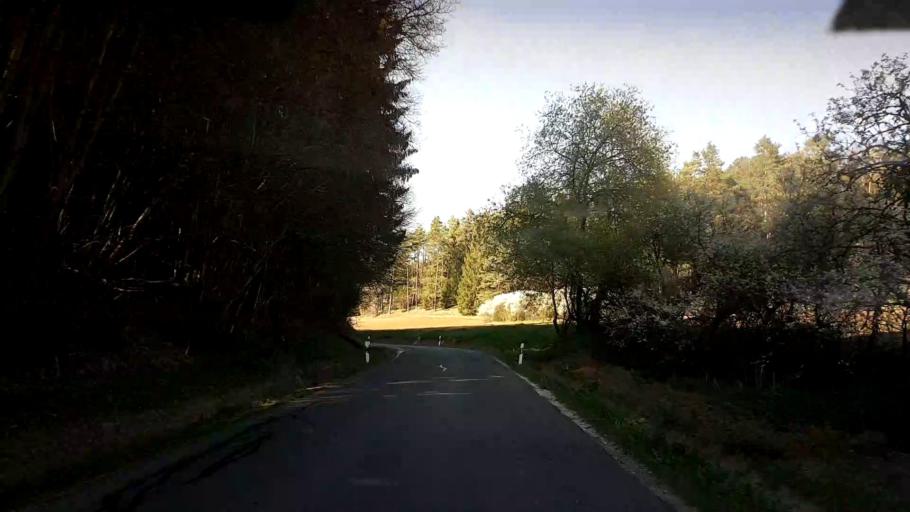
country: DE
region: Bavaria
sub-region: Upper Franconia
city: Waischenfeld
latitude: 49.8177
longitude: 11.3553
